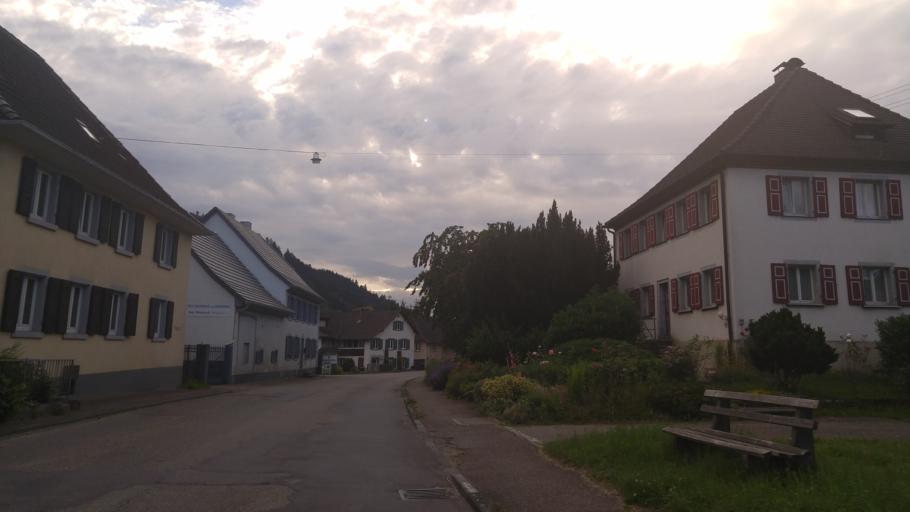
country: DE
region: Baden-Wuerttemberg
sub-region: Freiburg Region
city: Muenstertal/Schwarzwald
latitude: 47.8543
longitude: 7.7773
